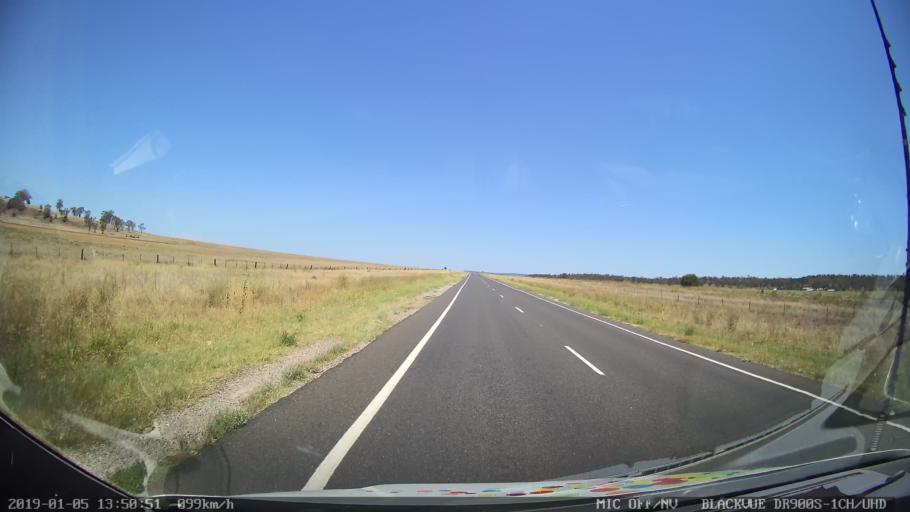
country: AU
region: New South Wales
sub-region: Gunnedah
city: Gunnedah
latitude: -31.0361
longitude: 150.2757
